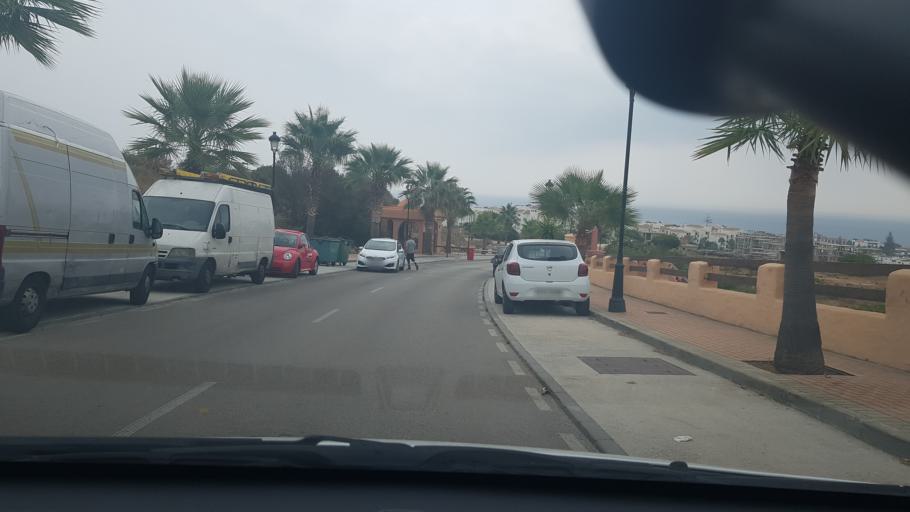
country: ES
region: Andalusia
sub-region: Provincia de Malaga
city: Manilva
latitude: 36.3648
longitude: -5.2376
